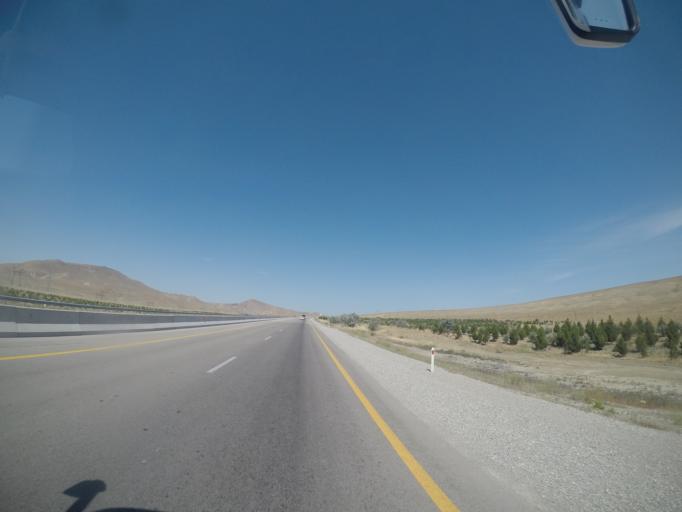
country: AZ
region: Sumqayit
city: Haci Zeynalabdin
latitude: 40.4994
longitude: 49.2939
